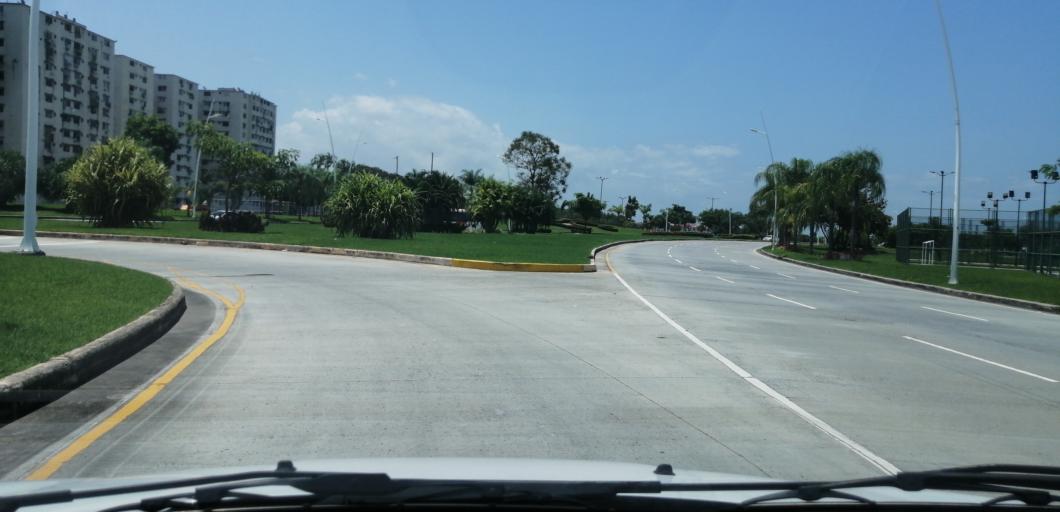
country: PA
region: Panama
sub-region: Distrito de Panama
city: Ancon
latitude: 8.9487
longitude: -79.5416
